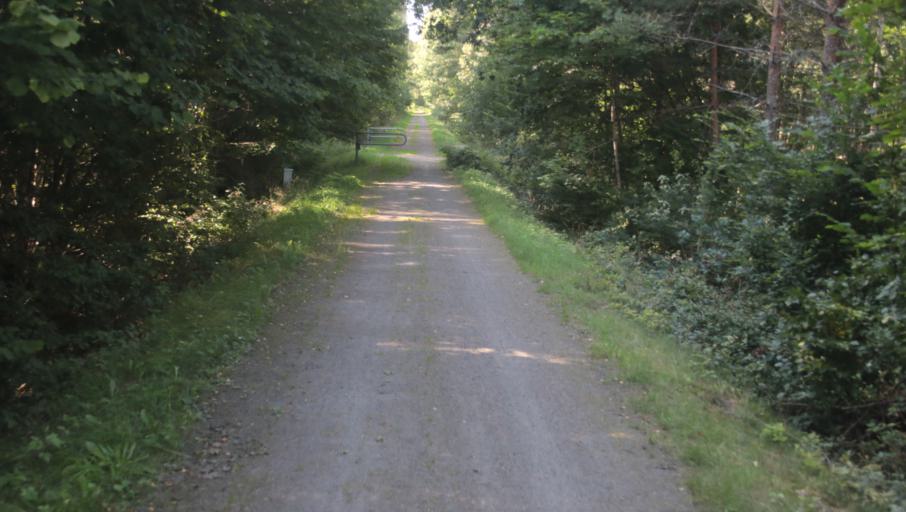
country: SE
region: Blekinge
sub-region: Karlshamns Kommun
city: Svangsta
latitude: 56.2866
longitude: 14.7505
